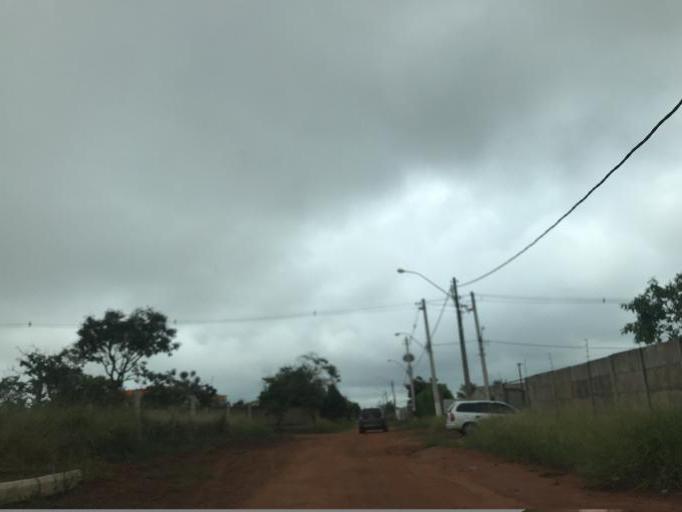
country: BR
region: Federal District
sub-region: Brasilia
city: Brasilia
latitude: -15.8253
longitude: -47.7889
